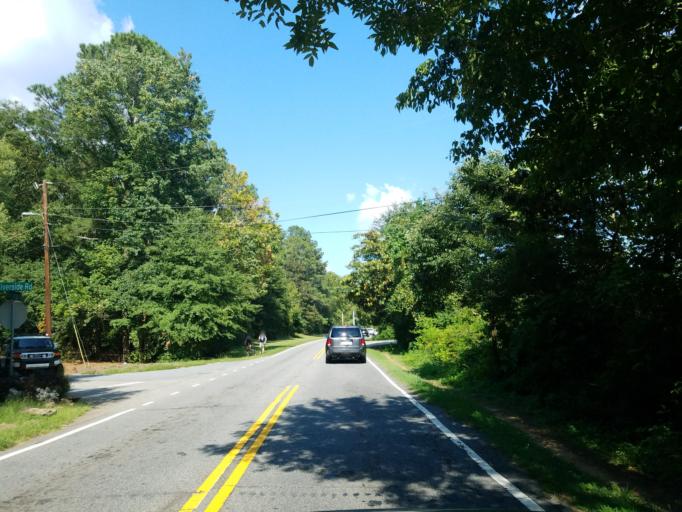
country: US
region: Georgia
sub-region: Fulton County
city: Roswell
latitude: 34.0067
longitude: -84.3492
